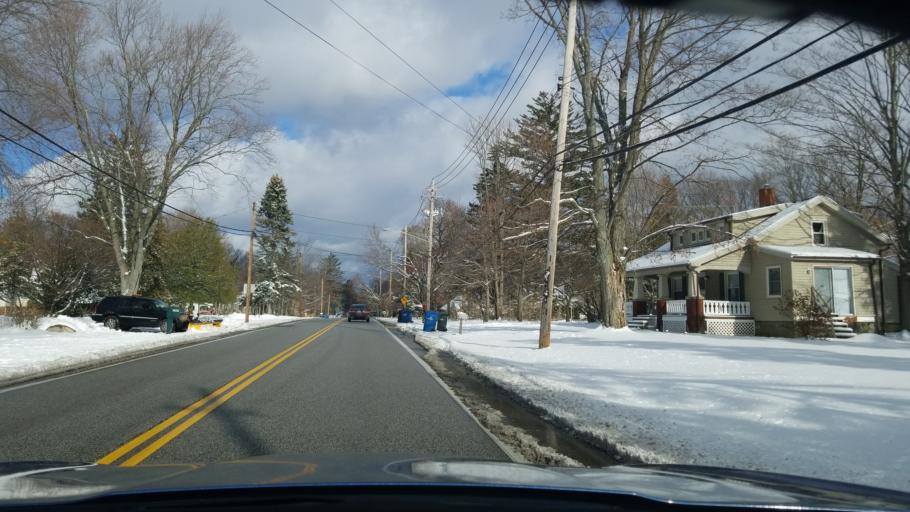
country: US
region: Ohio
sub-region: Cuyahoga County
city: North Olmsted
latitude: 41.4081
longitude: -81.8963
